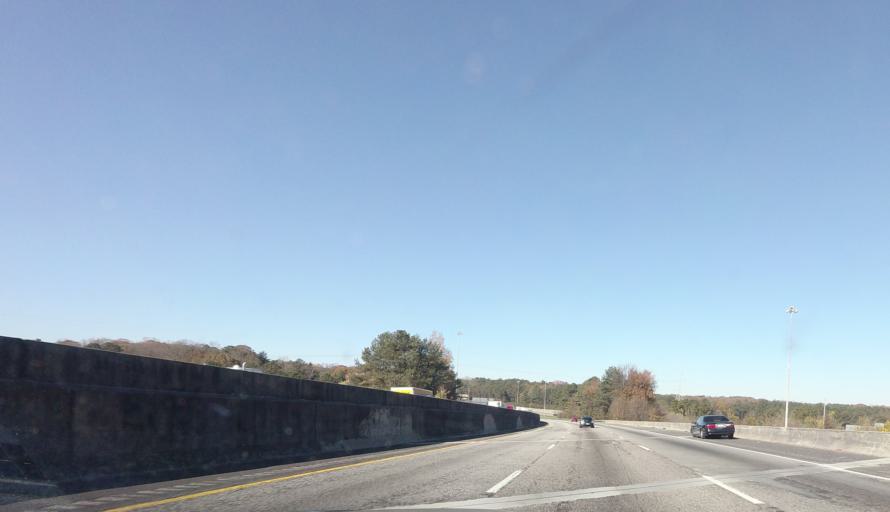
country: US
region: Georgia
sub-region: Fulton County
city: East Point
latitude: 33.7648
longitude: -84.4931
